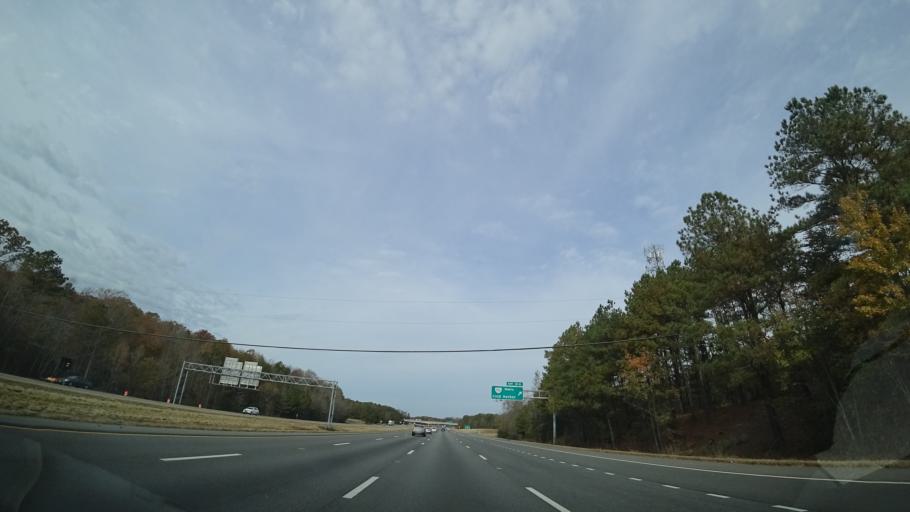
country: US
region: Virginia
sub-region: Henrico County
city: Sandston
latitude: 37.5445
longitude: -77.2824
